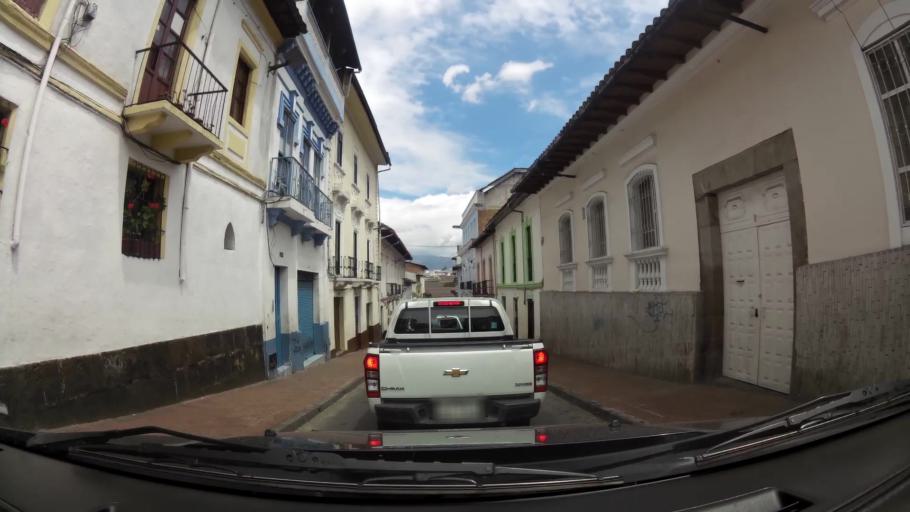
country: EC
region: Pichincha
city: Quito
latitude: -0.2163
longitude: -78.5129
